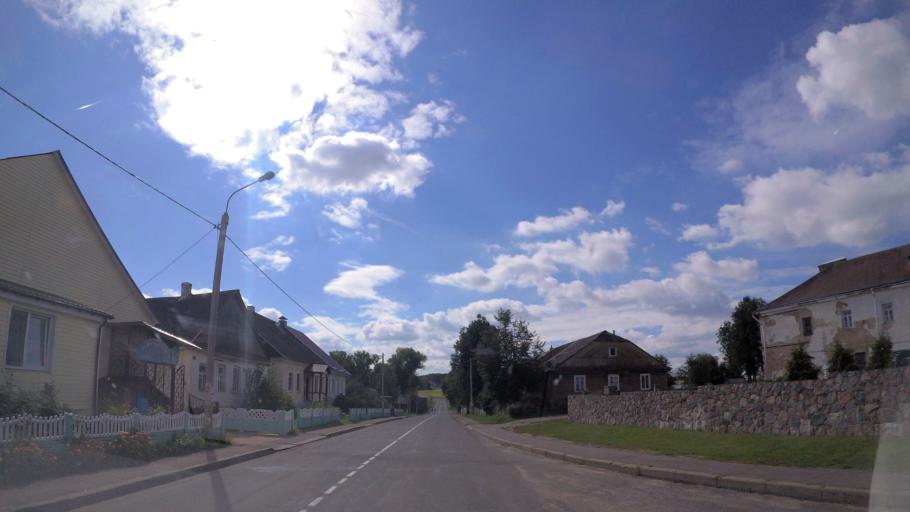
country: BY
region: Grodnenskaya
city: Hal'shany
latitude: 54.2565
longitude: 26.0104
